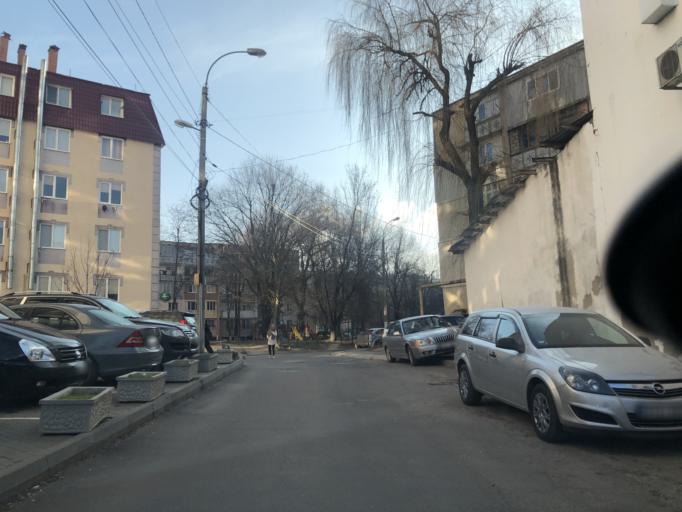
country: MD
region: Chisinau
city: Chisinau
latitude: 47.0333
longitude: 28.8658
